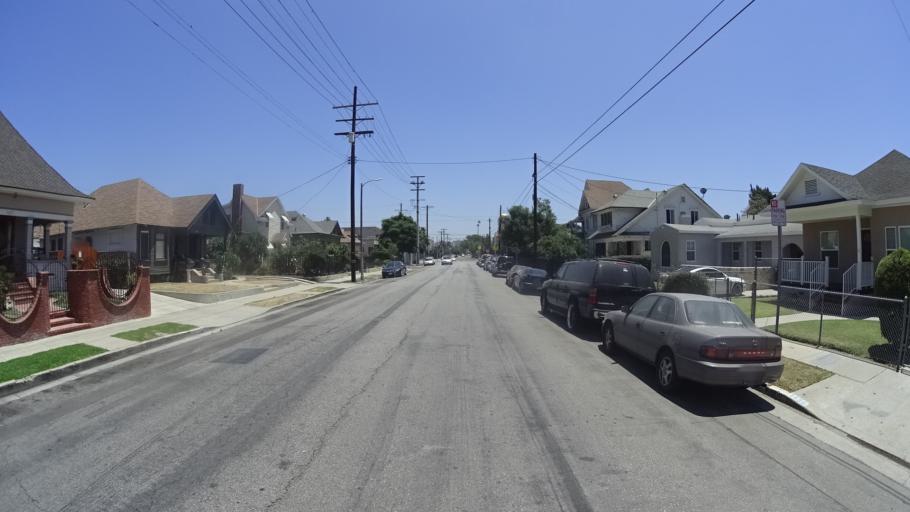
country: US
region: California
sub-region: Los Angeles County
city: View Park-Windsor Hills
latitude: 34.0241
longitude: -118.3034
